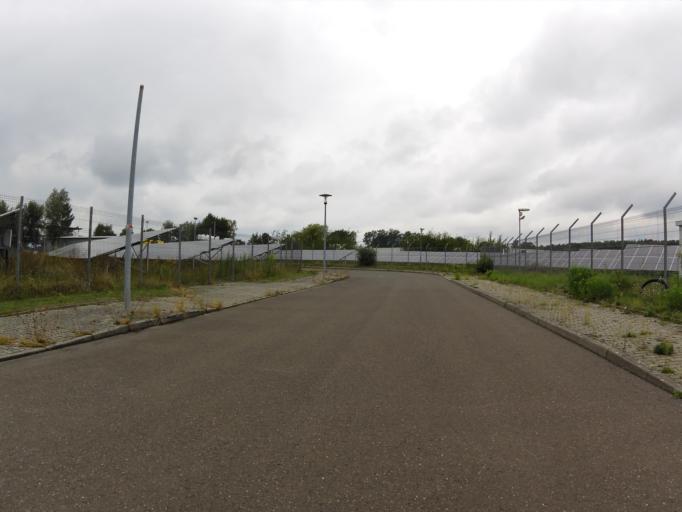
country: DE
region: Brandenburg
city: Storkow
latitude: 52.2687
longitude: 13.9458
